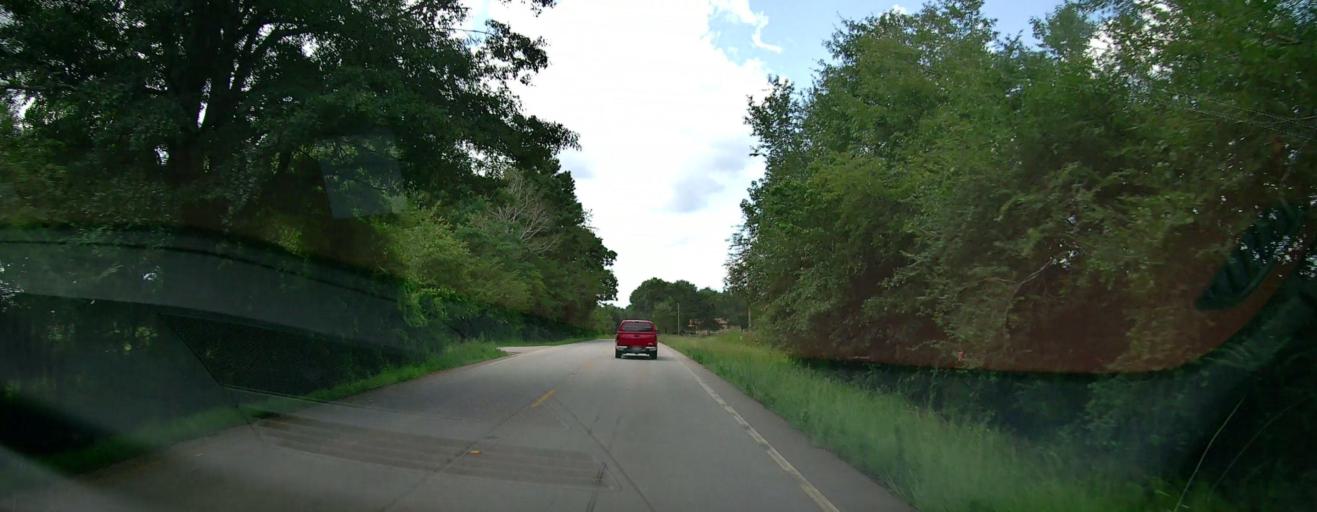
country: US
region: Georgia
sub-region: Meriwether County
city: Greenville
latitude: 33.0663
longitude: -84.7656
